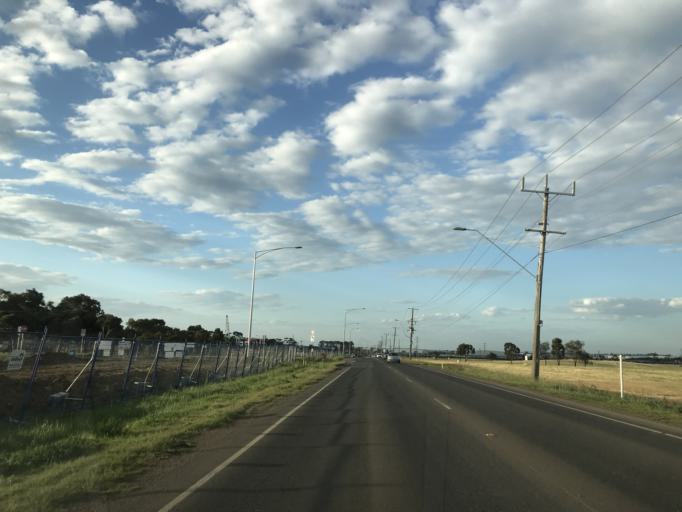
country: AU
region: Victoria
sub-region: Wyndham
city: Truganina
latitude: -37.8295
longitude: 144.7483
